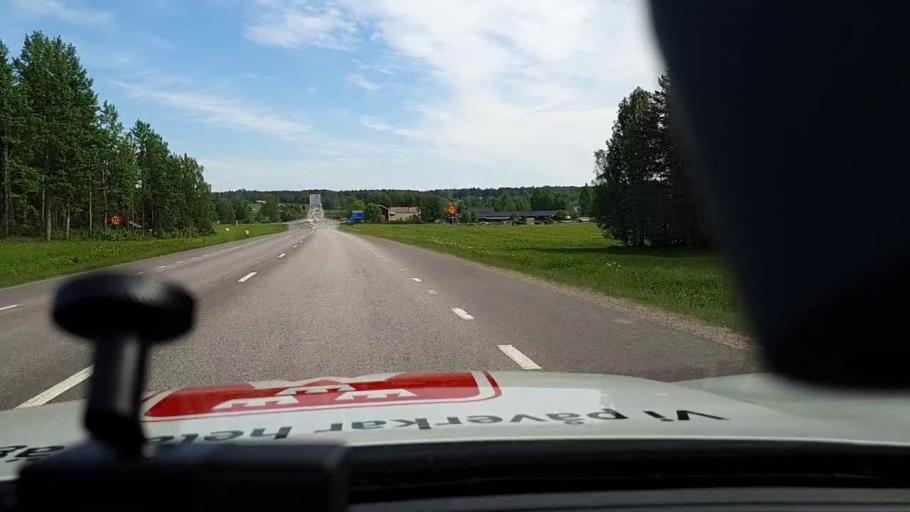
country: SE
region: Norrbotten
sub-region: Lulea Kommun
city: Gammelstad
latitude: 65.5843
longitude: 22.0228
